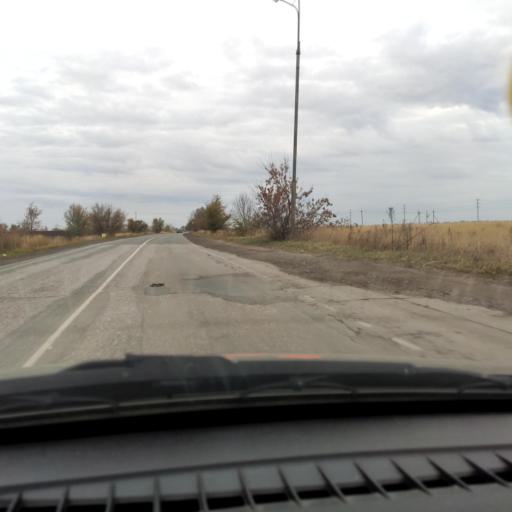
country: RU
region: Samara
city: Podstepki
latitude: 53.5166
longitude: 49.2144
